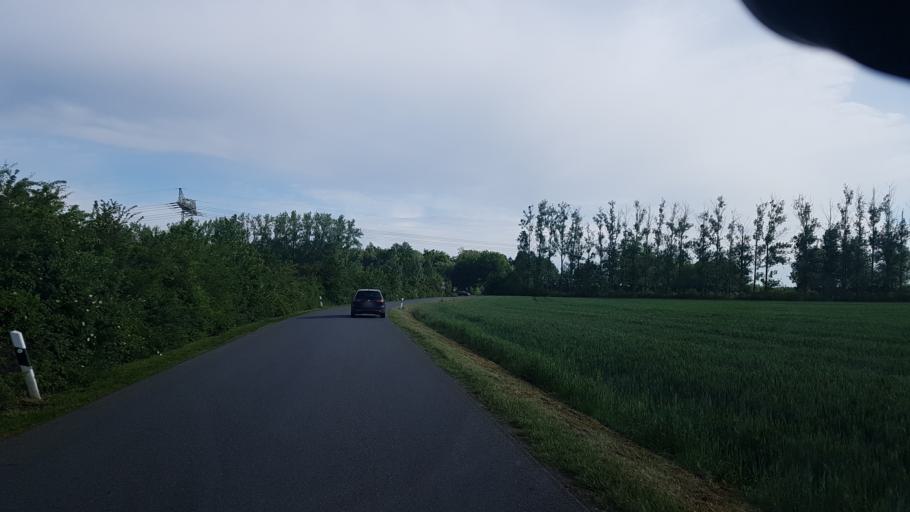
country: DE
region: Brandenburg
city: Luckau
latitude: 51.8388
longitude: 13.7508
